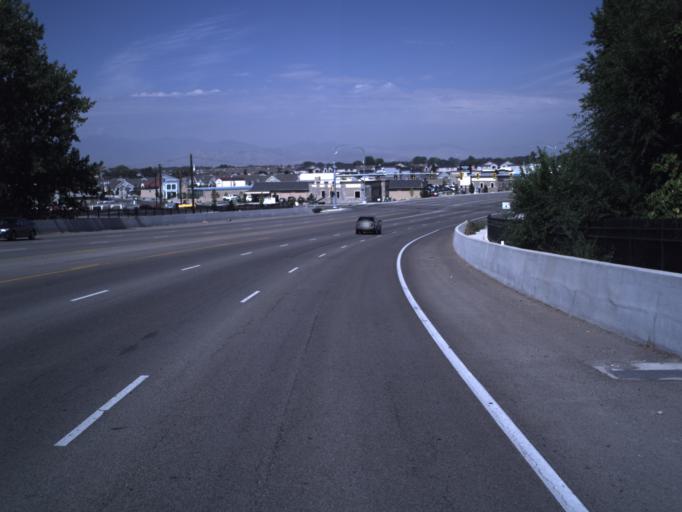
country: US
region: Utah
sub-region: Utah County
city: Pleasant Grove
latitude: 40.3602
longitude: -111.7451
